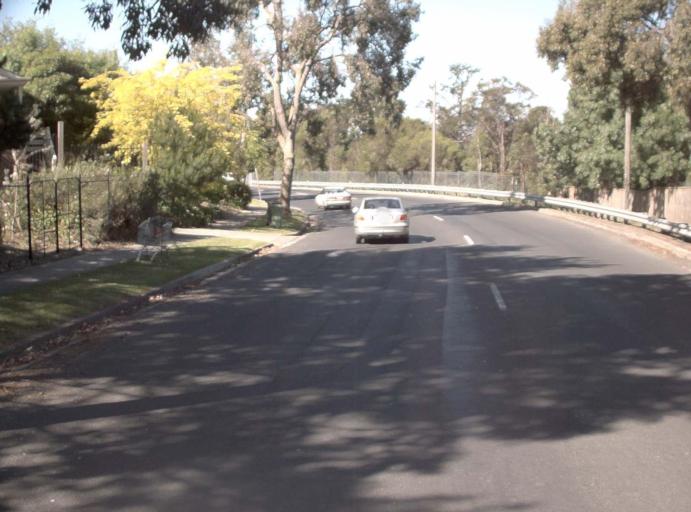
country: AU
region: Victoria
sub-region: Maroondah
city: Croydon South
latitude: -37.7997
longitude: 145.2736
